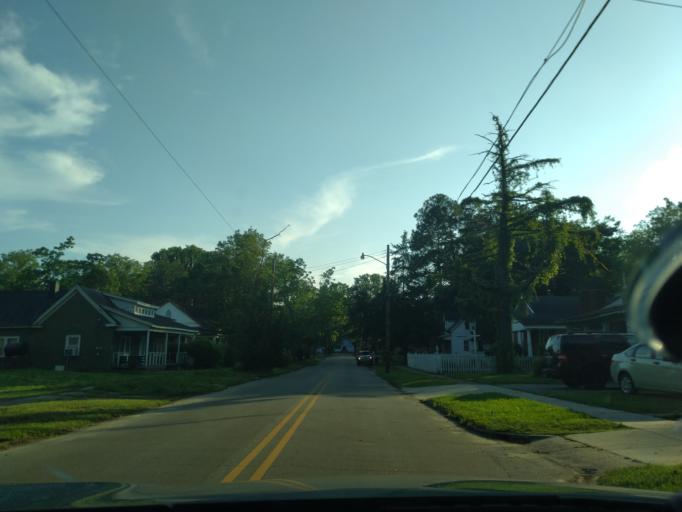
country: US
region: North Carolina
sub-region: Washington County
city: Plymouth
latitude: 35.8642
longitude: -76.7513
